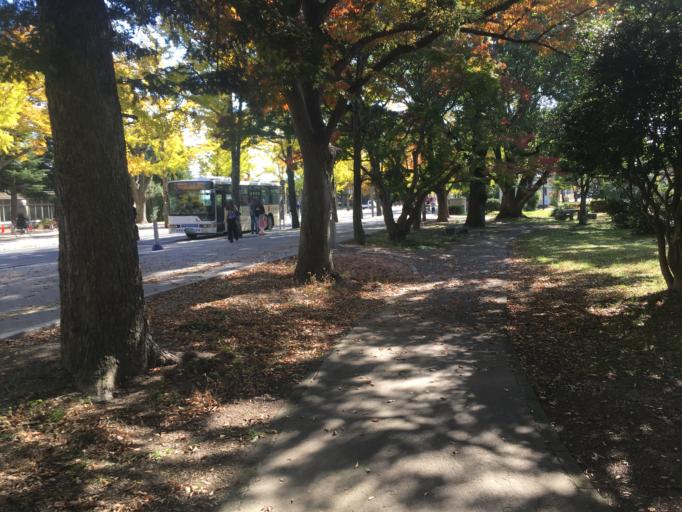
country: JP
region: Okayama
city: Okayama-shi
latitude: 34.6874
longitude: 133.9195
